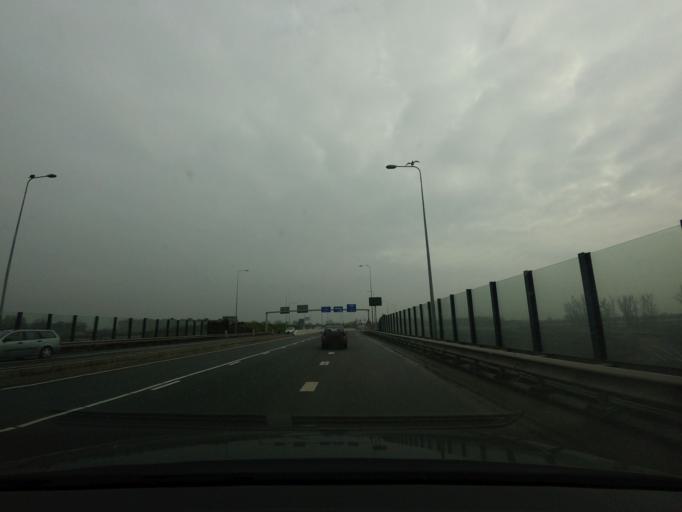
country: NL
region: North Holland
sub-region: Gemeente Amsterdam
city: Amsterdam-Zuidoost
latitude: 52.3103
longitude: 4.9692
